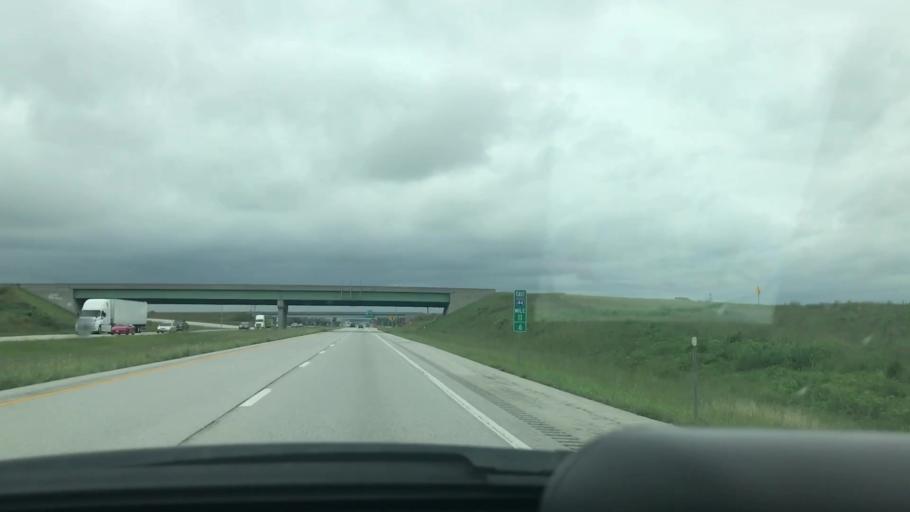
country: US
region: Missouri
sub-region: Jasper County
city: Duenweg
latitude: 37.0597
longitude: -94.4318
